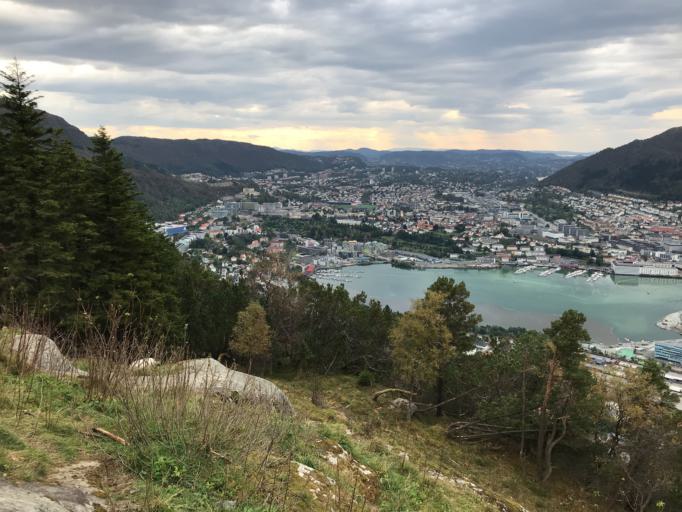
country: NO
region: Hordaland
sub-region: Bergen
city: Bergen
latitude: 60.3934
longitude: 5.3447
